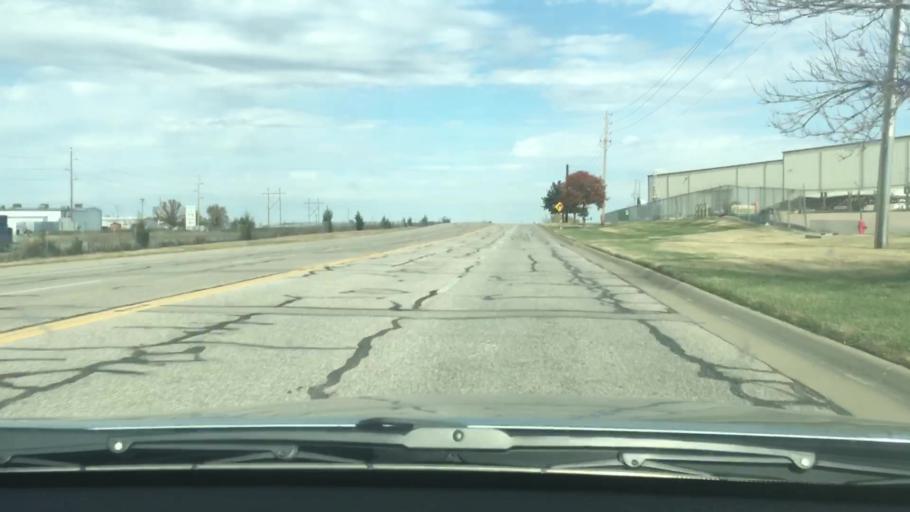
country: US
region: Kansas
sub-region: Sedgwick County
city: Wichita
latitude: 37.6311
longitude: -97.2878
